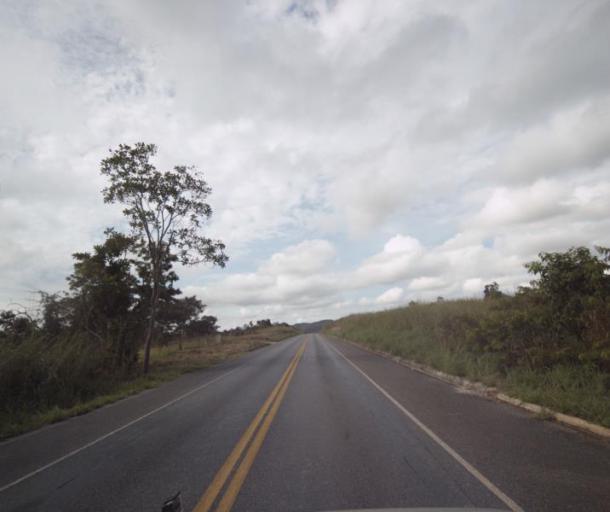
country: BR
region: Goias
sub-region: Pirenopolis
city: Pirenopolis
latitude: -15.5583
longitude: -48.6227
